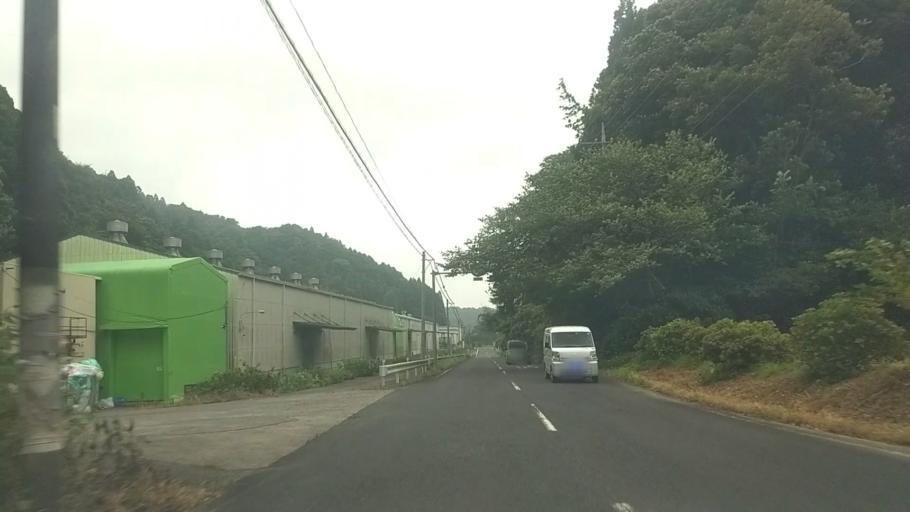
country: JP
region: Chiba
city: Katsuura
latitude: 35.2500
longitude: 140.2436
